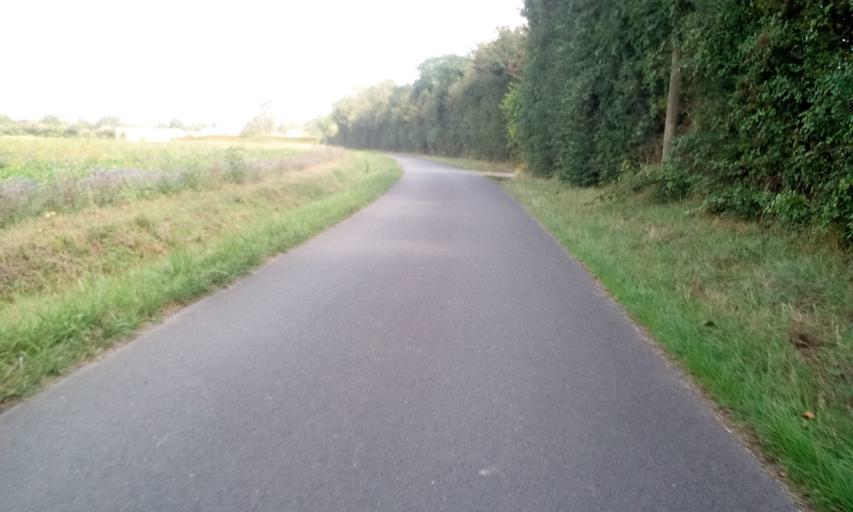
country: FR
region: Lower Normandy
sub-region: Departement du Calvados
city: Argences
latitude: 49.1324
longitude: -0.1187
